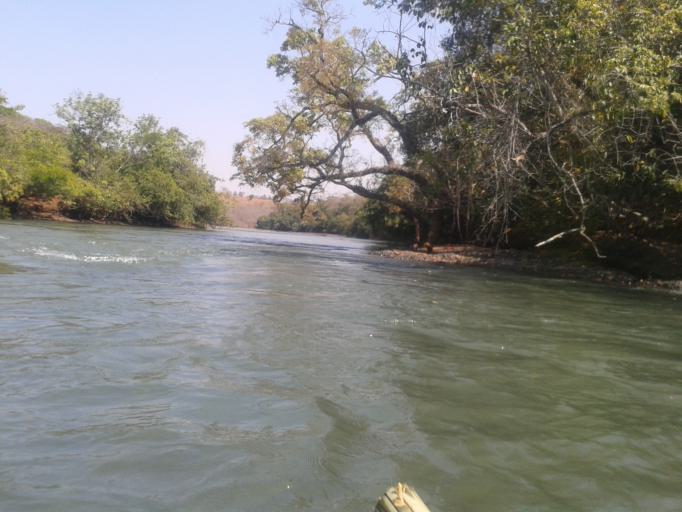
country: BR
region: Minas Gerais
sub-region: Ituiutaba
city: Ituiutaba
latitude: -18.9451
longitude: -49.4300
